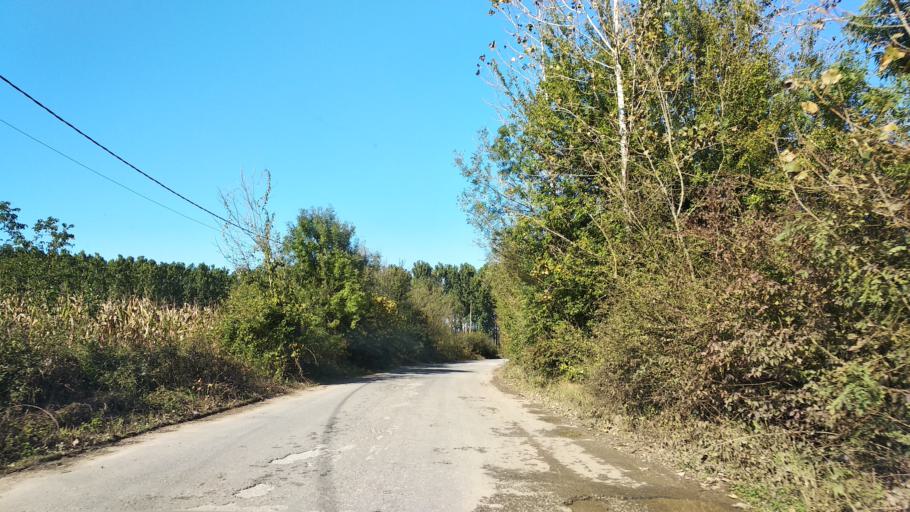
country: TR
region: Sakarya
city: Ortakoy
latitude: 41.0294
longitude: 30.6070
